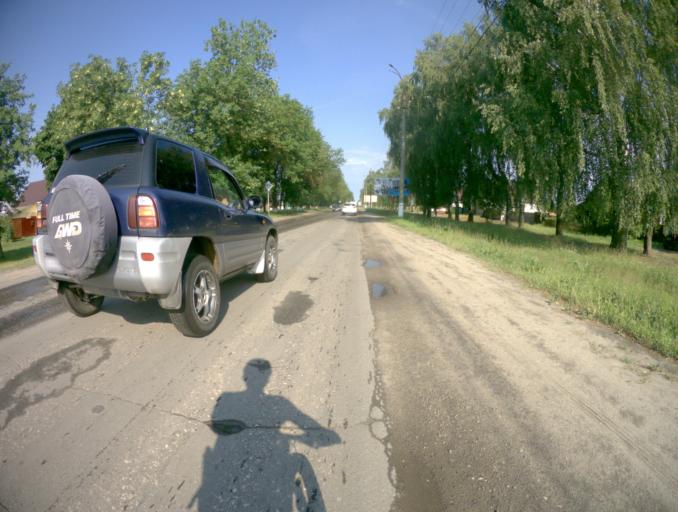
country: RU
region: Vladimir
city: Vyazniki
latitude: 56.2346
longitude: 42.1875
